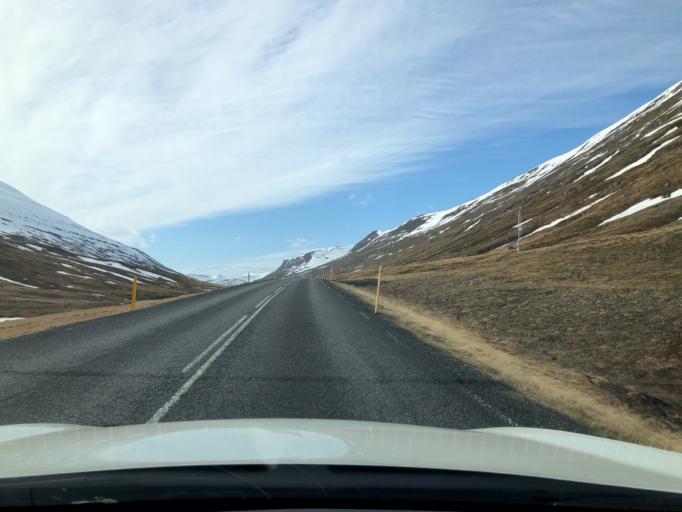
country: IS
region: East
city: Egilsstadir
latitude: 65.1692
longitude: -14.3382
